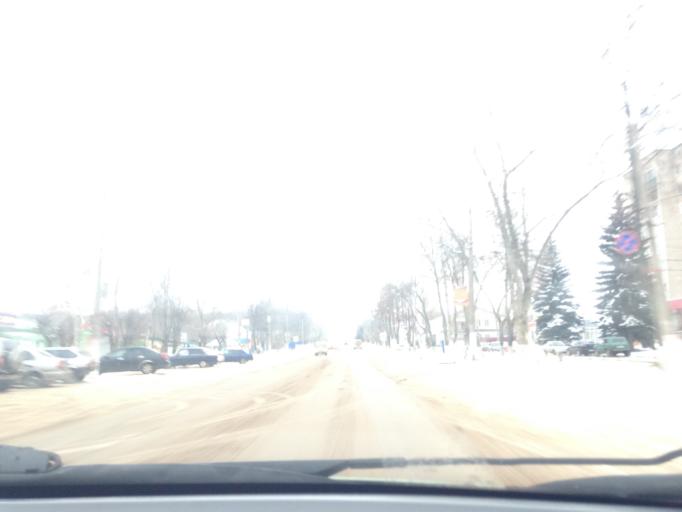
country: RU
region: Tula
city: Shchekino
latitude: 54.0060
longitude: 37.5123
